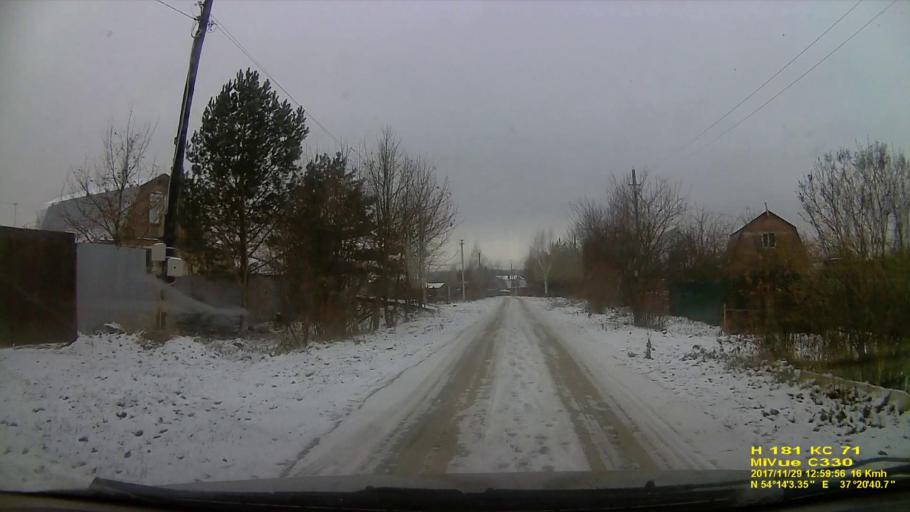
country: RU
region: Tula
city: Leninskiy
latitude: 54.2343
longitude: 37.3443
